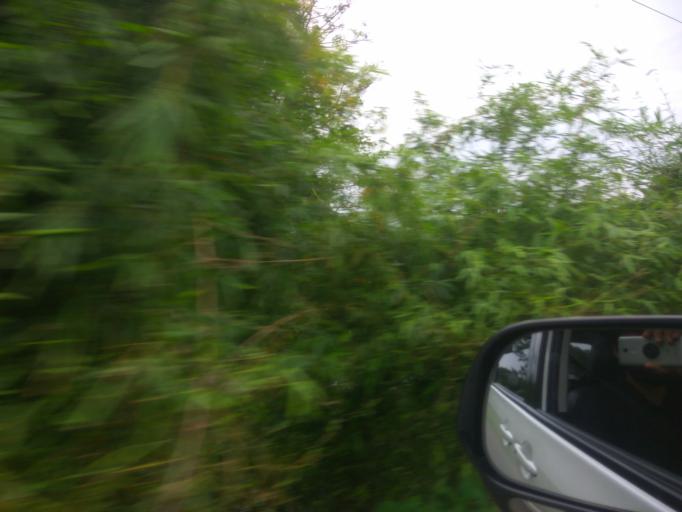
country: IN
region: Assam
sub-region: Karimganj
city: Karimganj
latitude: 24.9497
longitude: 92.2407
